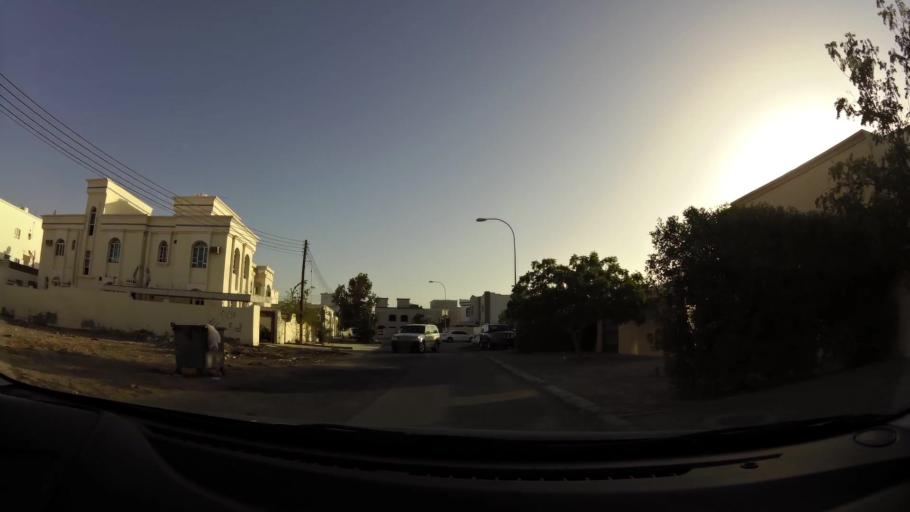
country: OM
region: Muhafazat Masqat
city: As Sib al Jadidah
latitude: 23.6093
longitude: 58.2247
